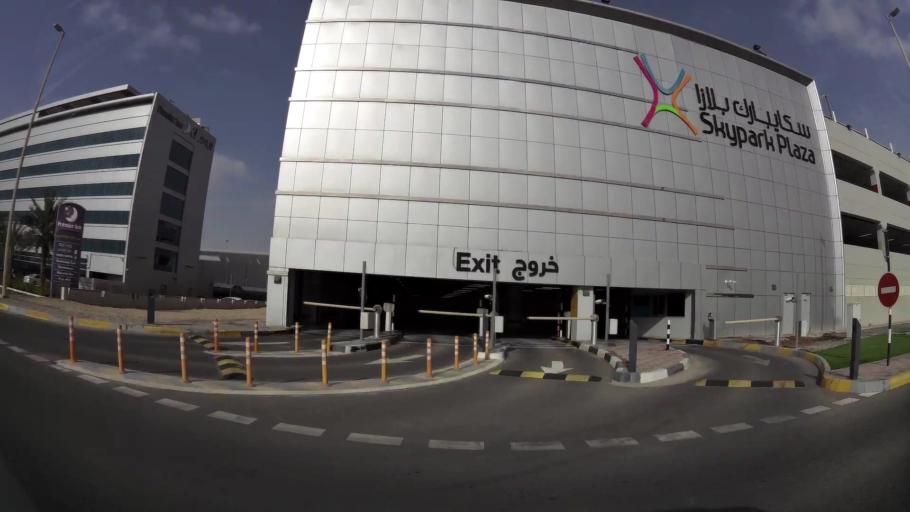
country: AE
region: Abu Dhabi
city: Abu Dhabi
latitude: 24.4278
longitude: 54.6418
